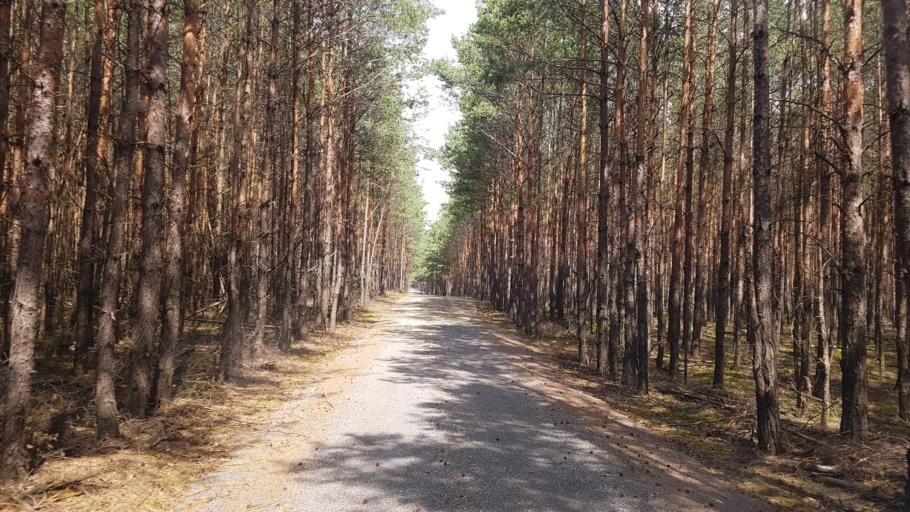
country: DE
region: Brandenburg
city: Crinitz
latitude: 51.7034
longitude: 13.8202
